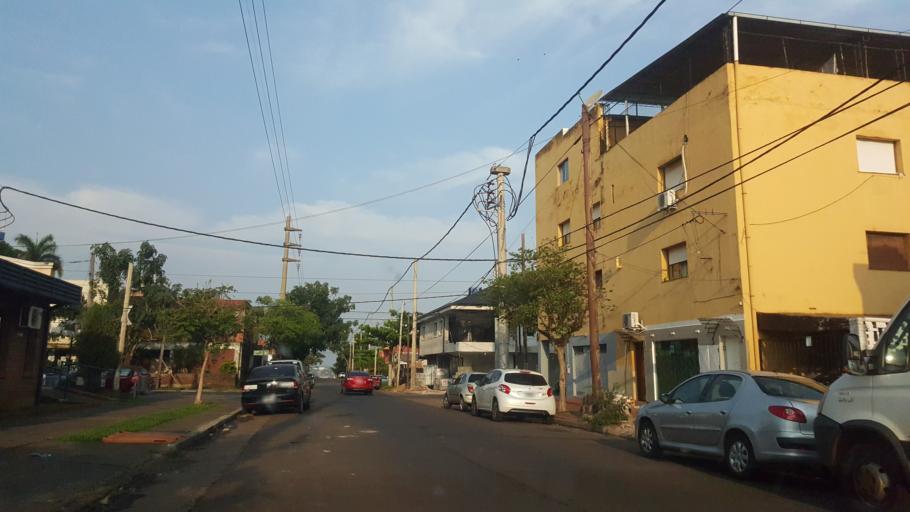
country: AR
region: Misiones
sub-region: Departamento de Capital
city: Posadas
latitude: -27.3591
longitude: -55.8941
